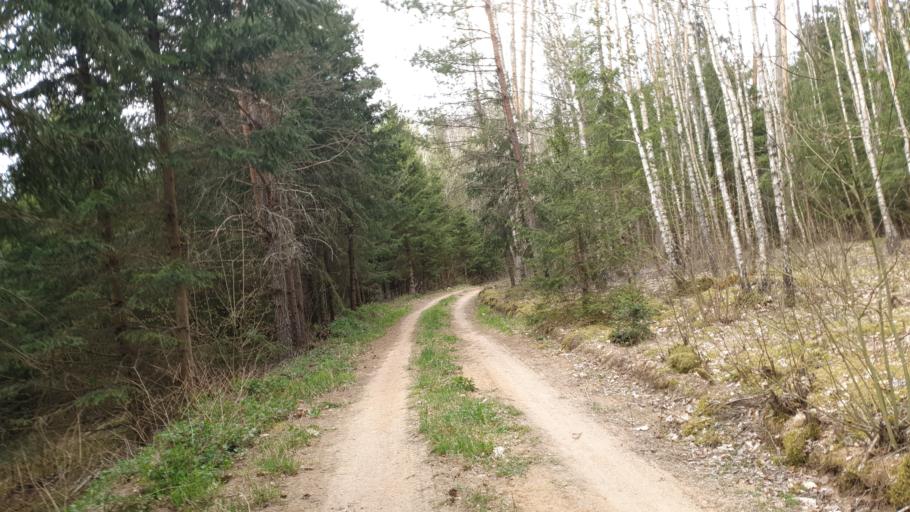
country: LT
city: Aukstadvaris
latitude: 54.5136
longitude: 24.6416
